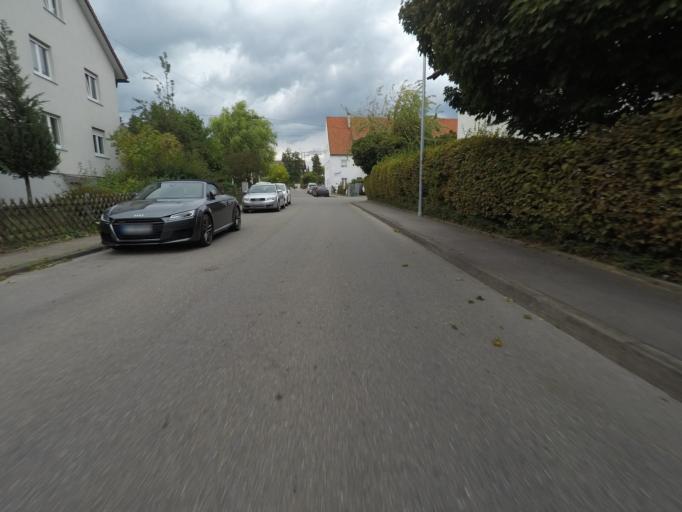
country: DE
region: Baden-Wuerttemberg
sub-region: Regierungsbezirk Stuttgart
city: Filderstadt
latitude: 48.6562
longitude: 9.1997
